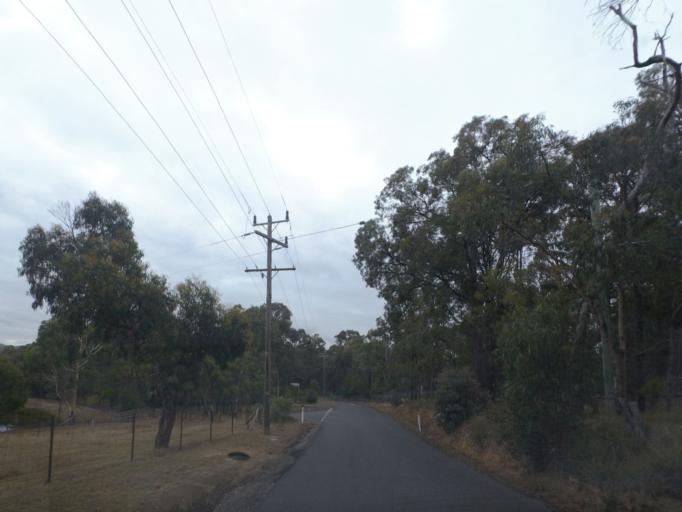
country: AU
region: Victoria
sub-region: Nillumbik
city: Saint Andrews
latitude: -37.6207
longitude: 145.2642
